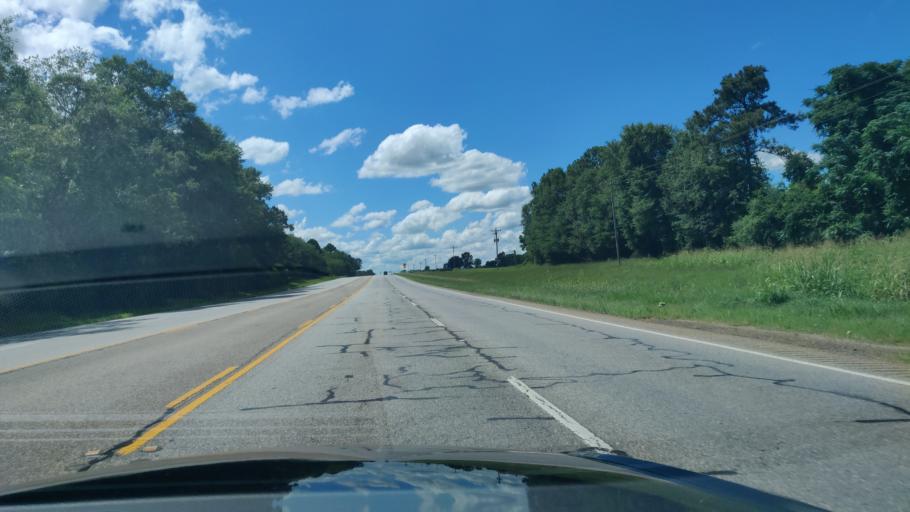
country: US
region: Georgia
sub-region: Stewart County
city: Richland
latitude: 31.9821
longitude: -84.6228
